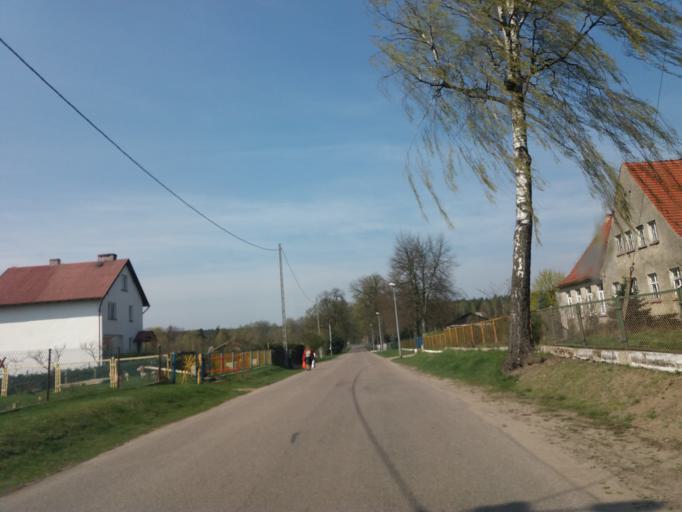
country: PL
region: West Pomeranian Voivodeship
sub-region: Powiat choszczenski
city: Recz
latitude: 53.1894
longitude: 15.6436
